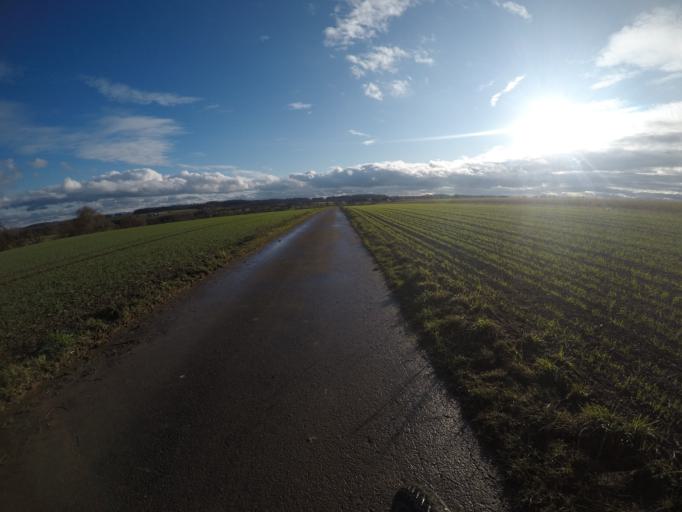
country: DE
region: Baden-Wuerttemberg
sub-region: Regierungsbezirk Stuttgart
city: Bondorf
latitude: 48.5389
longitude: 8.8741
